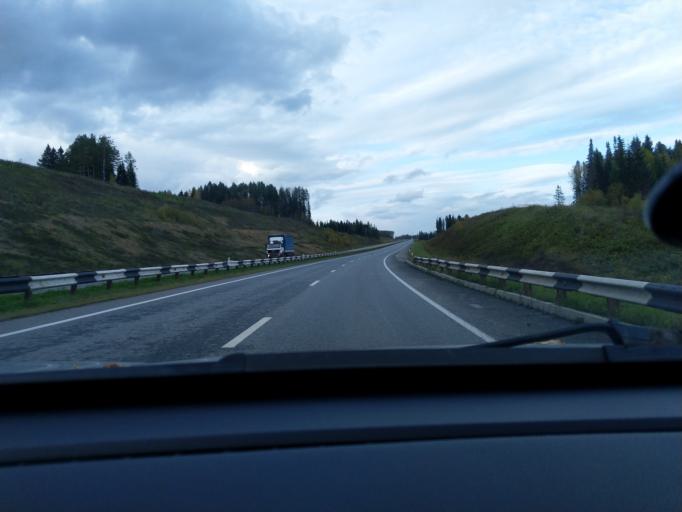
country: RU
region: Perm
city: Polazna
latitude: 58.3198
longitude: 56.4672
